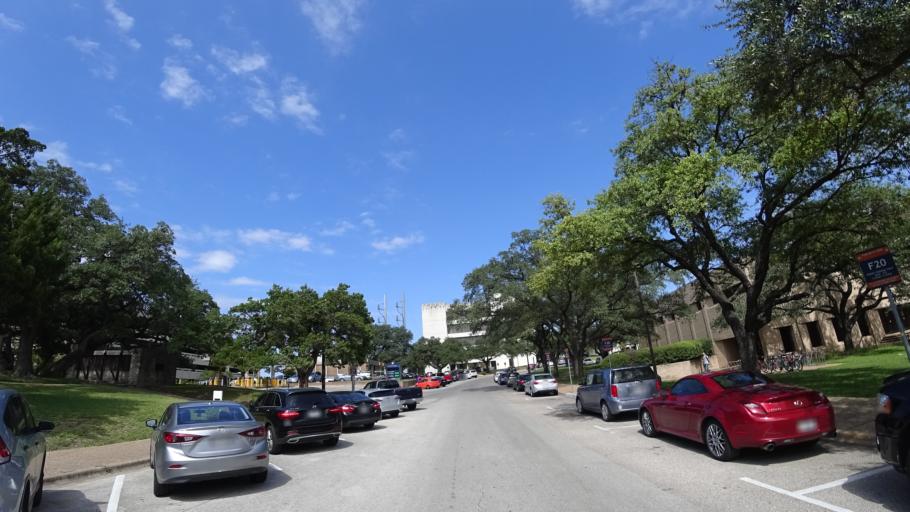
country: US
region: Texas
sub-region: Travis County
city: Austin
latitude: 30.2871
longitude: -97.7319
